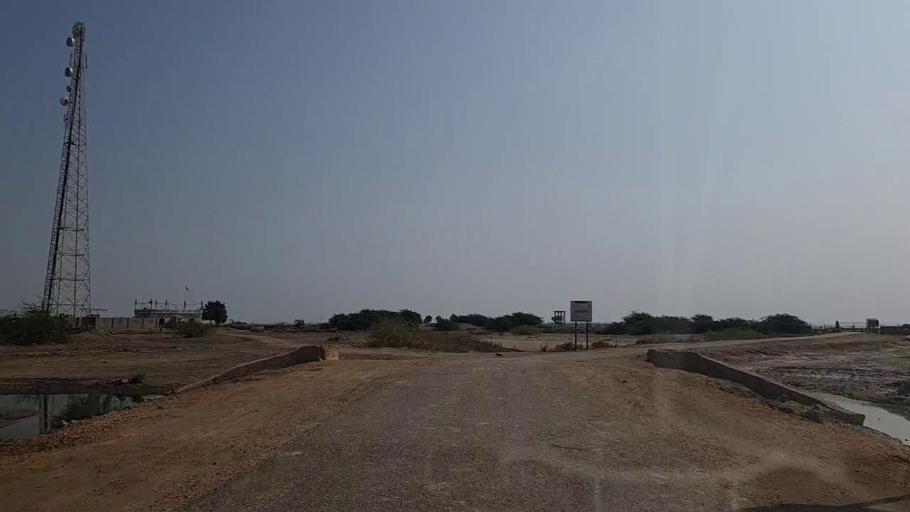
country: PK
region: Sindh
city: Chuhar Jamali
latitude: 24.1648
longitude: 67.9001
